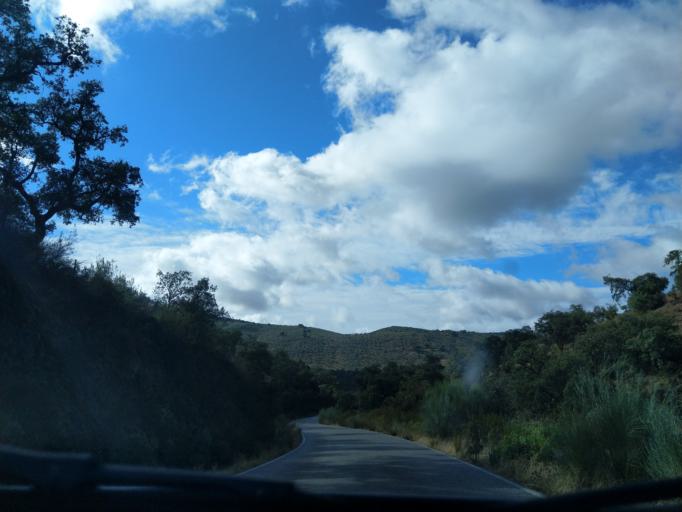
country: ES
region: Extremadura
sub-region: Provincia de Badajoz
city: Reina
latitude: 38.1356
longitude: -5.9166
